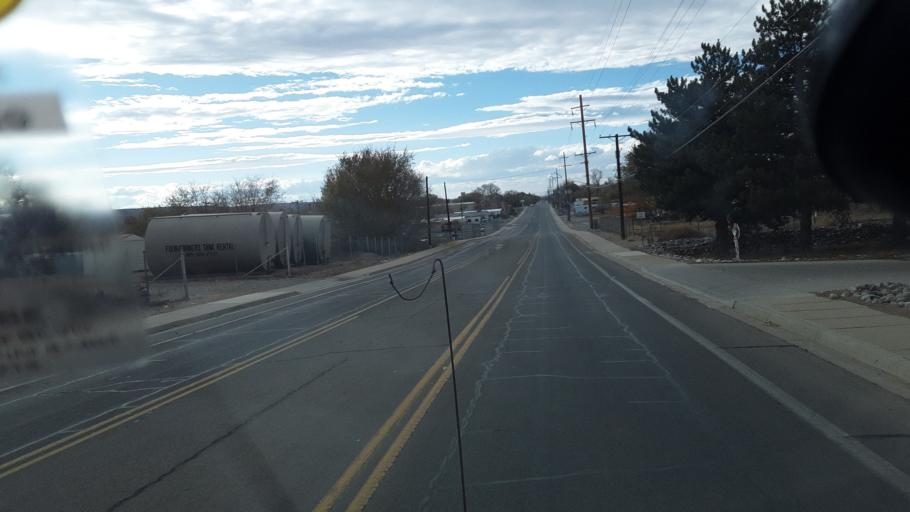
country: US
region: New Mexico
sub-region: San Juan County
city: Farmington
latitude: 36.7265
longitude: -108.1669
